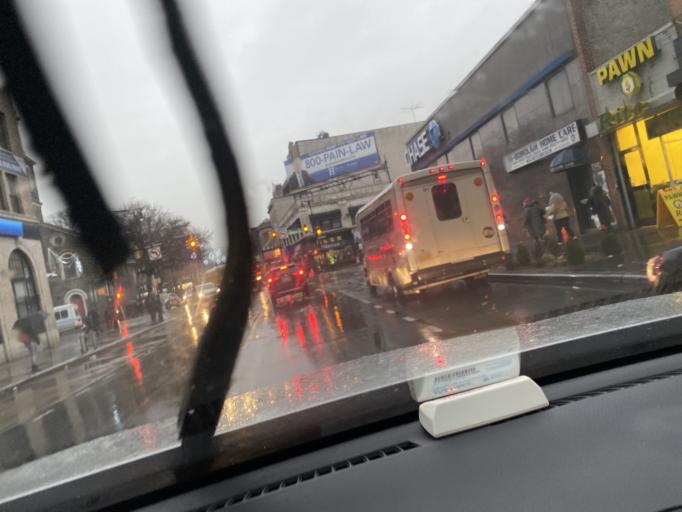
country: US
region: New York
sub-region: Kings County
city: Brooklyn
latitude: 40.6505
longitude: -73.9581
